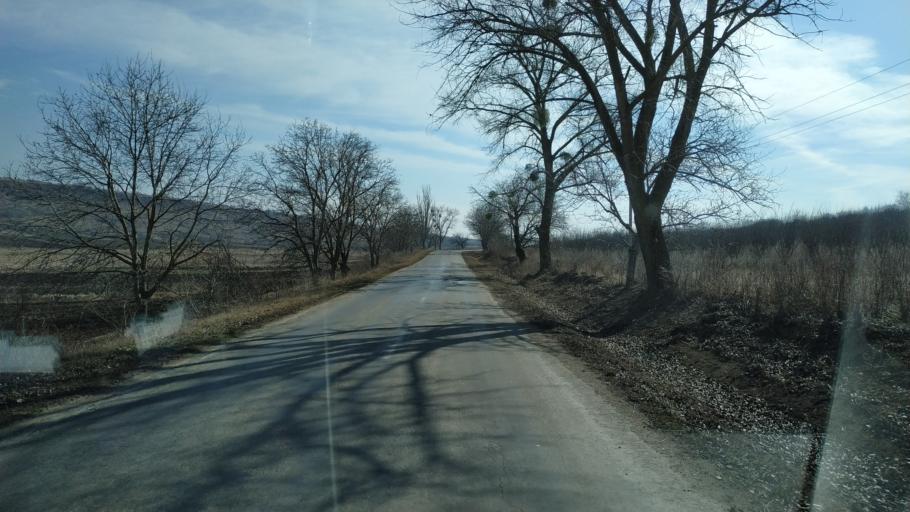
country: MD
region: Nisporeni
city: Nisporeni
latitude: 47.1331
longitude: 28.1195
